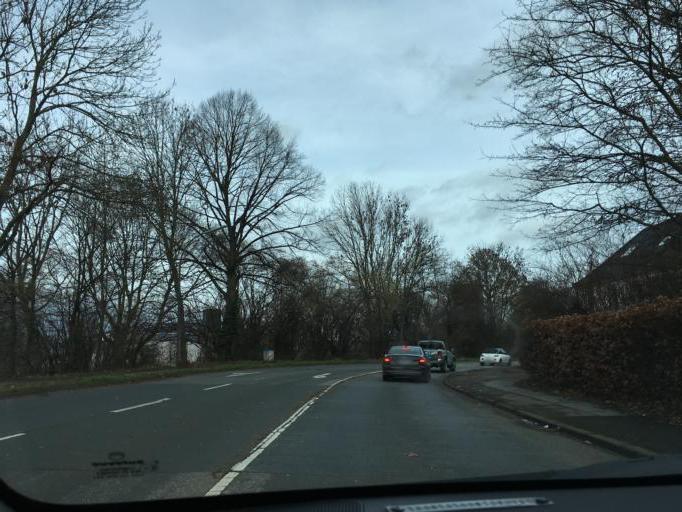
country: DE
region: North Rhine-Westphalia
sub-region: Regierungsbezirk Arnsberg
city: Dortmund
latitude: 51.4744
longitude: 7.4880
